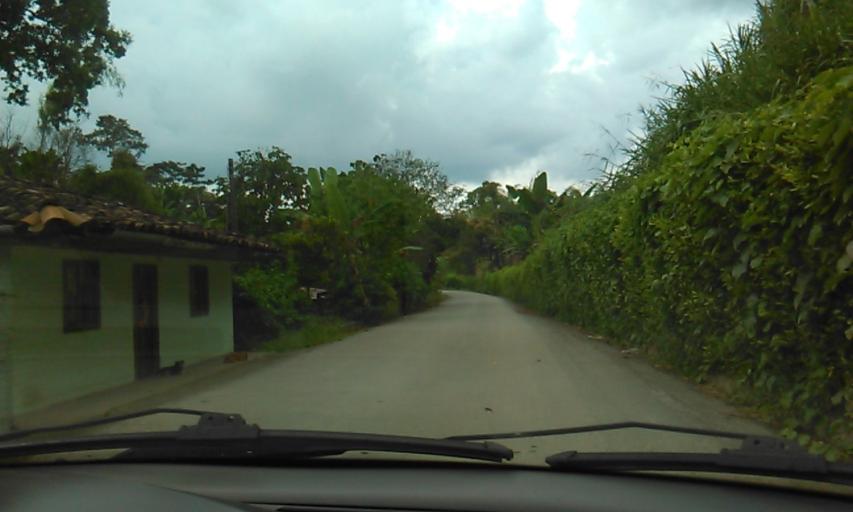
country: CO
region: Quindio
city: La Tebaida
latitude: 4.5164
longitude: -75.8334
